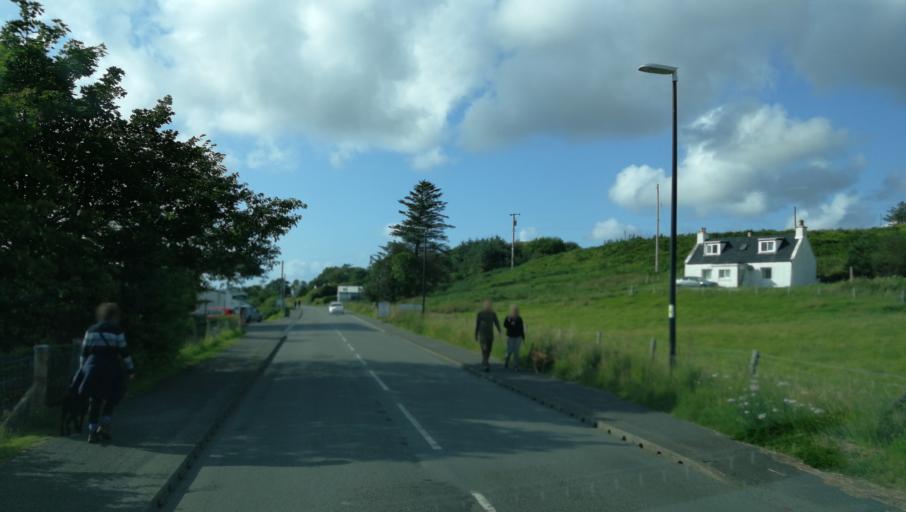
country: GB
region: Scotland
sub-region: Highland
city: Isle of Skye
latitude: 57.4328
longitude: -6.5746
